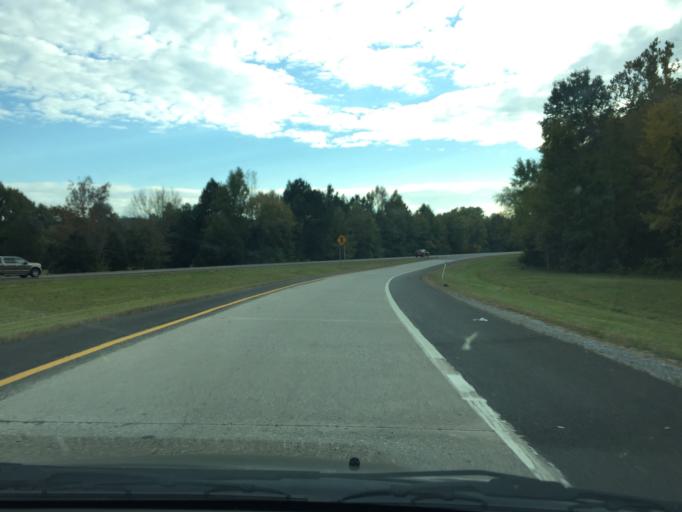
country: US
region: Tennessee
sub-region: Monroe County
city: Sweetwater
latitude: 35.6217
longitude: -84.4942
